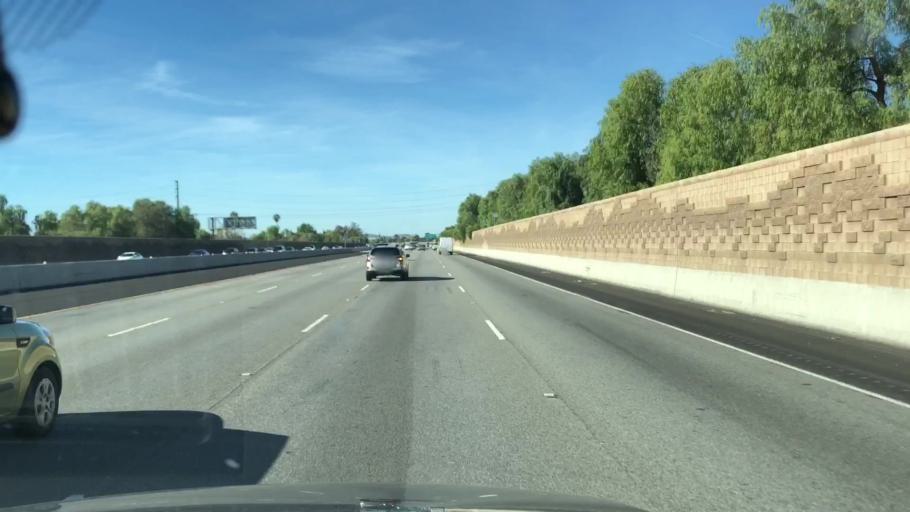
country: US
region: California
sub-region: Ventura County
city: Santa Susana
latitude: 34.2819
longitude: -118.7067
